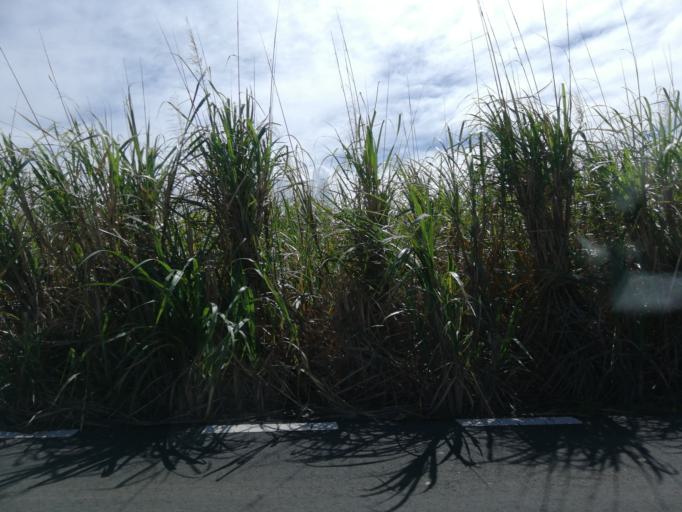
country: MU
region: Grand Port
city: Plaine Magnien
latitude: -20.4536
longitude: 57.6746
